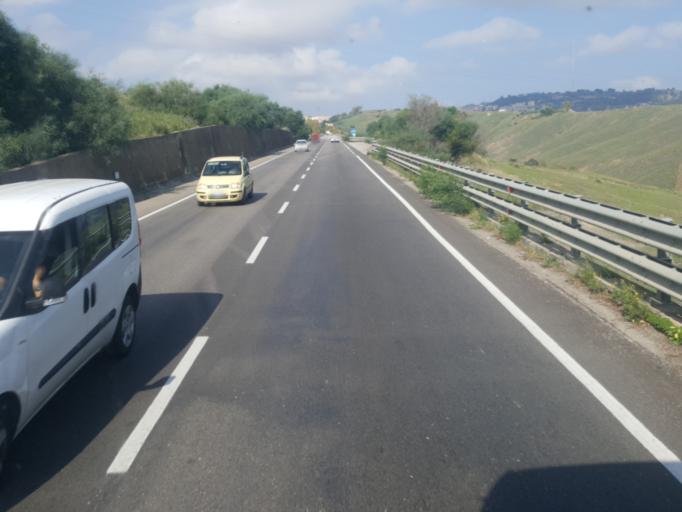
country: IT
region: Sicily
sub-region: Provincia di Caltanissetta
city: Caltanissetta
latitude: 37.4718
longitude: 14.0941
